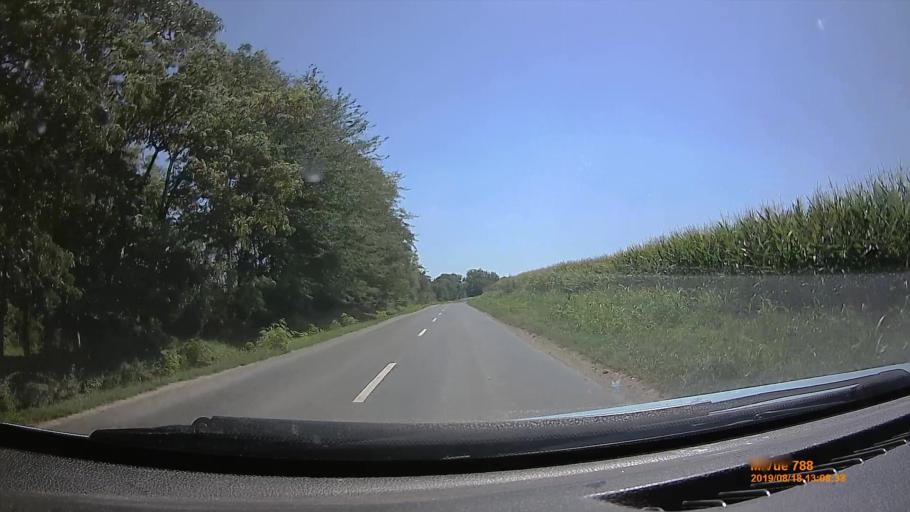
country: HU
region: Fejer
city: Kaloz
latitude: 46.9365
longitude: 18.5043
